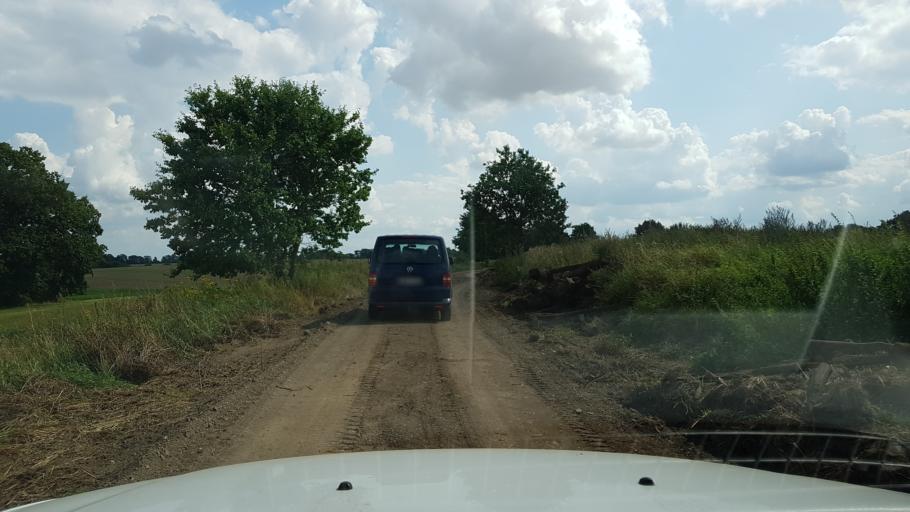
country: PL
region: West Pomeranian Voivodeship
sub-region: Powiat choszczenski
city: Pelczyce
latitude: 53.0763
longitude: 15.3092
